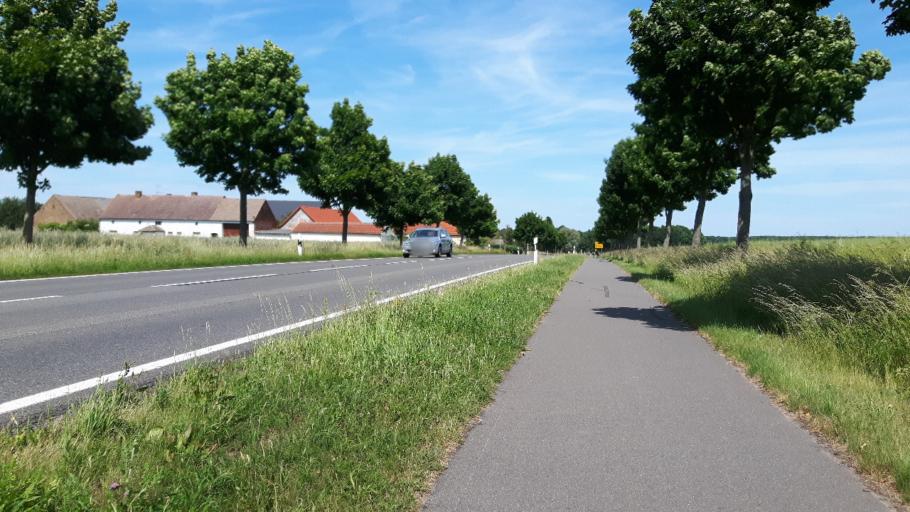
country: DE
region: Saxony-Anhalt
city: Kropstadt
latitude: 52.0236
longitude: 12.7966
